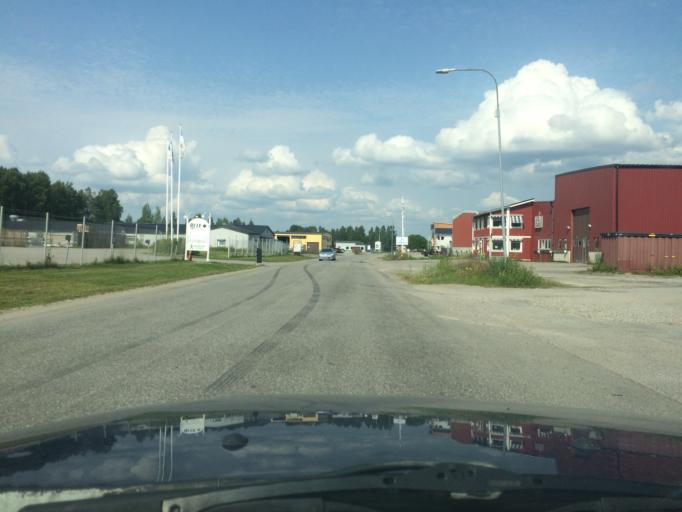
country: SE
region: Norrbotten
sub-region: Pitea Kommun
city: Bergsviken
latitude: 65.3359
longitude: 21.4167
